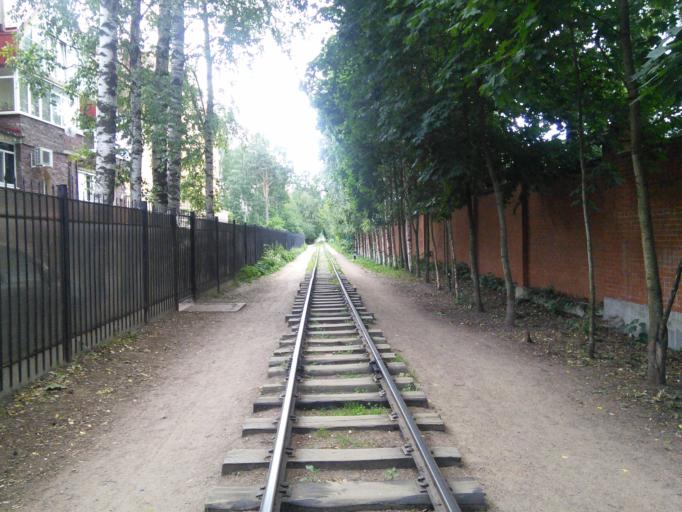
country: RU
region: St.-Petersburg
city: Kolomyagi
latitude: 60.0317
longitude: 30.2911
